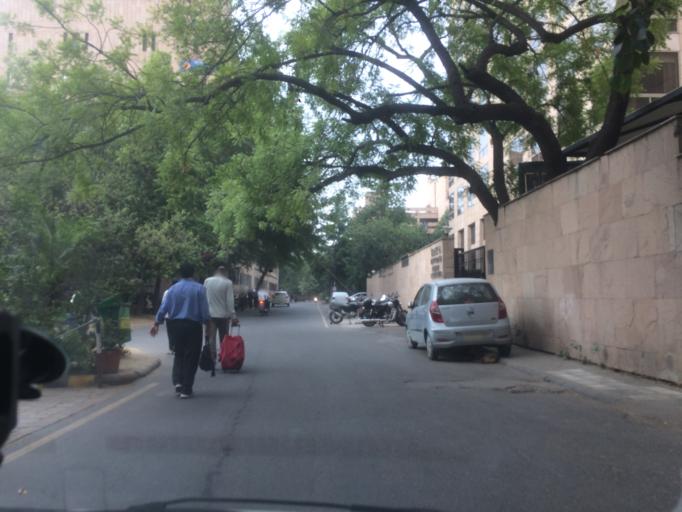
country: IN
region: NCT
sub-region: New Delhi
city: New Delhi
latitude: 28.5687
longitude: 77.1858
